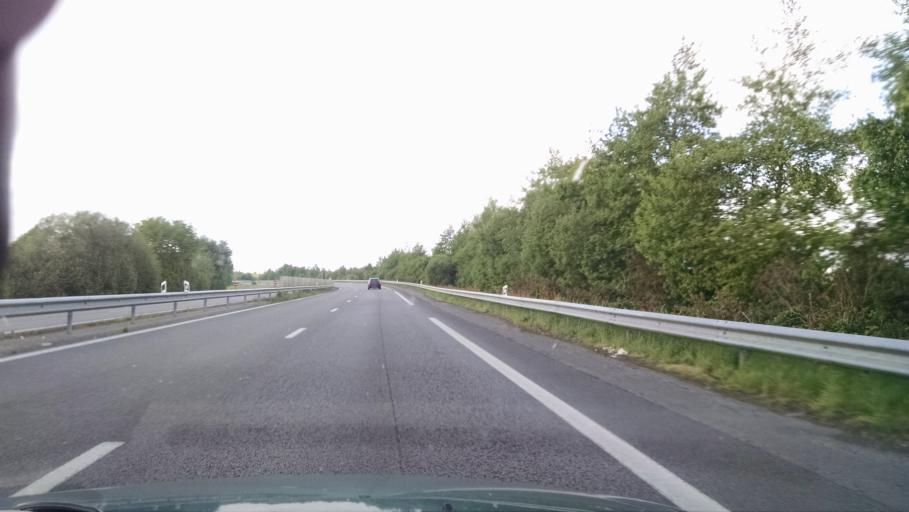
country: FR
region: Brittany
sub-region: Departement du Finistere
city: Taule
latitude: 48.5990
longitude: -3.8876
